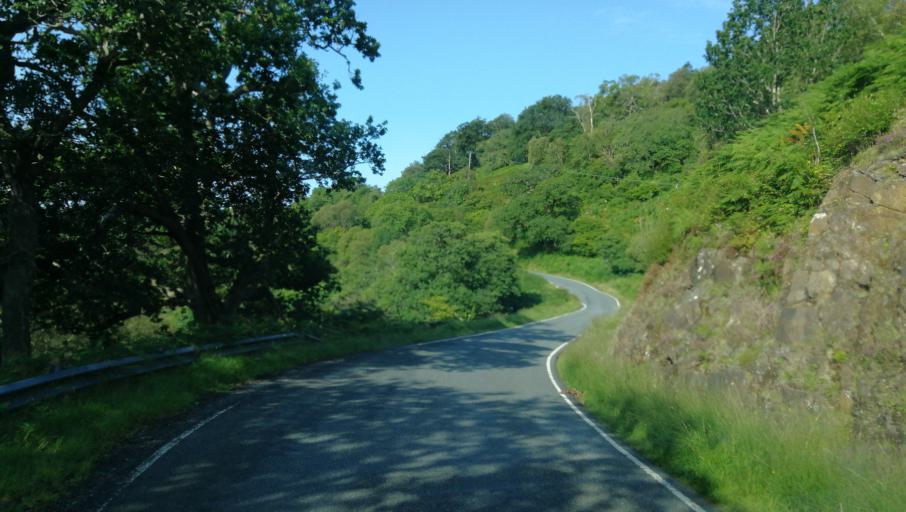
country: GB
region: Scotland
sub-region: Argyll and Bute
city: Isle Of Mull
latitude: 56.6808
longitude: -5.8289
